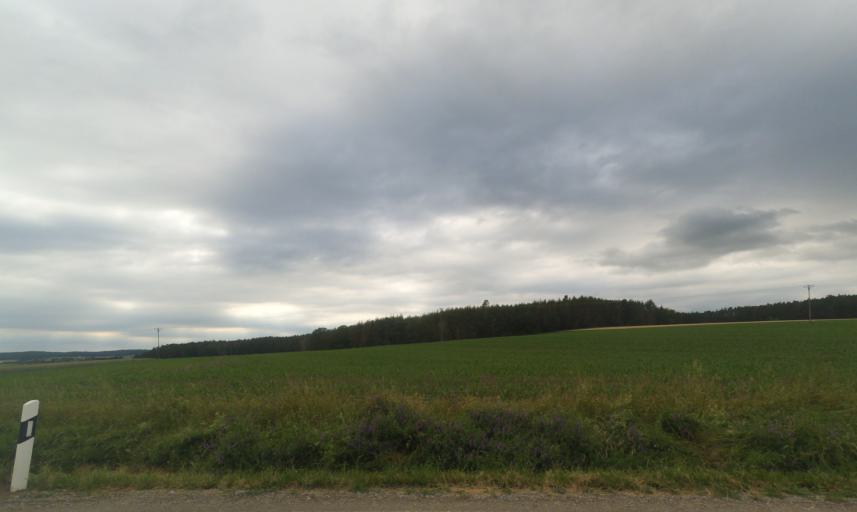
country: DE
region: Bavaria
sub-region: Regierungsbezirk Mittelfranken
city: Burghaslach
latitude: 49.7035
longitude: 10.5897
